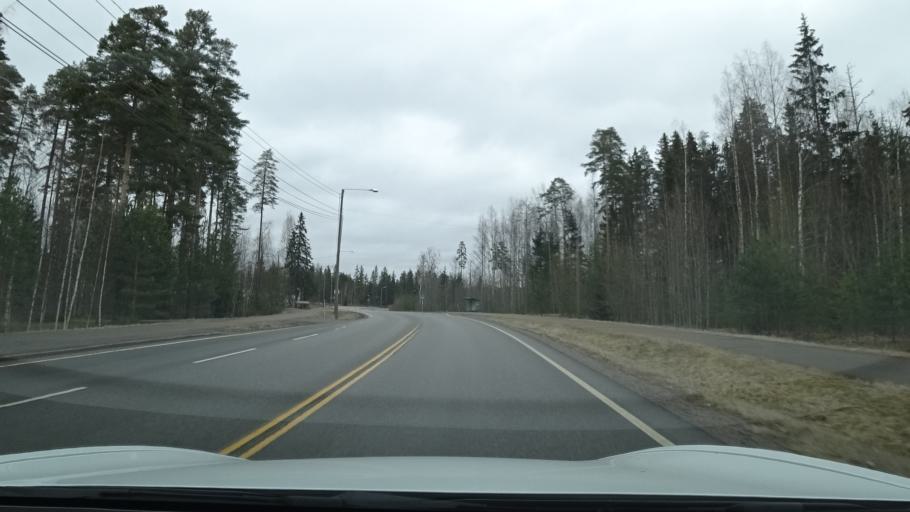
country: FI
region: Uusimaa
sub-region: Porvoo
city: Askola
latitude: 60.5029
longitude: 25.5636
